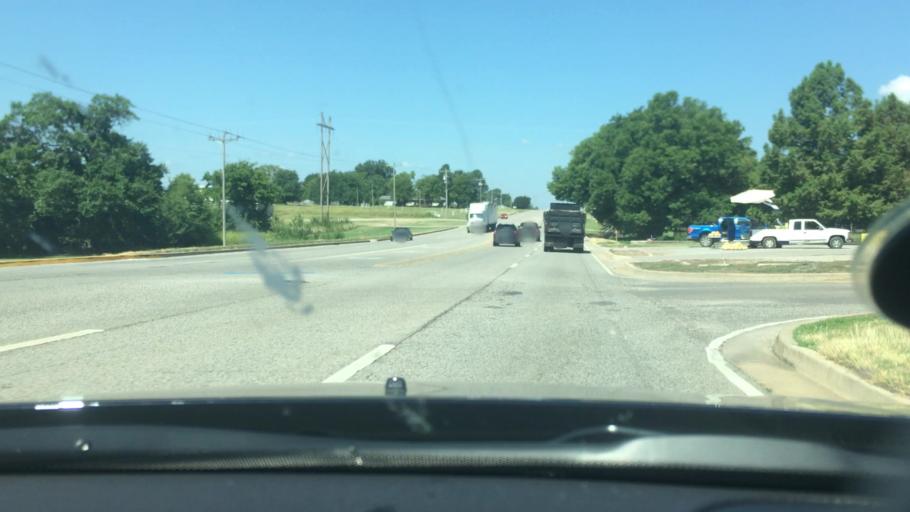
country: US
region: Oklahoma
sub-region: Bryan County
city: Calera
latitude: 33.9983
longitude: -96.5002
